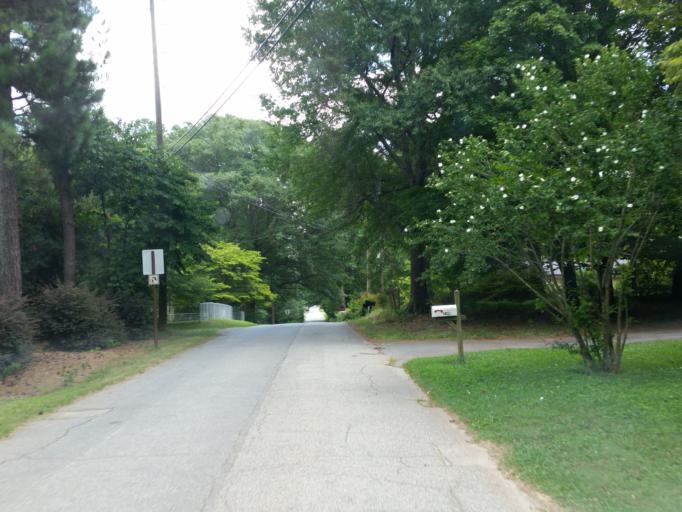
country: US
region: Georgia
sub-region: Cobb County
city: Marietta
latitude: 33.9974
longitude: -84.5218
